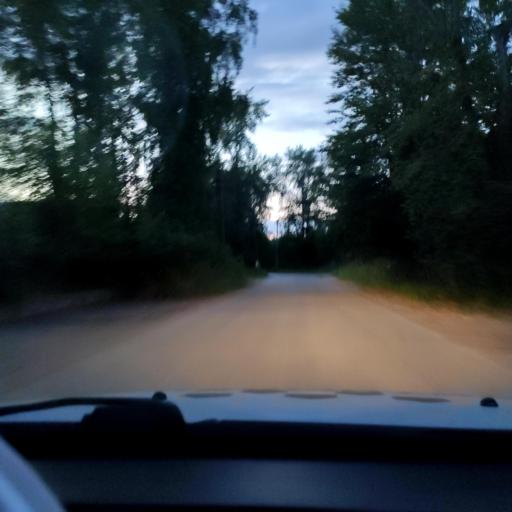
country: RU
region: Perm
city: Overyata
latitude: 58.0126
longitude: 55.9422
